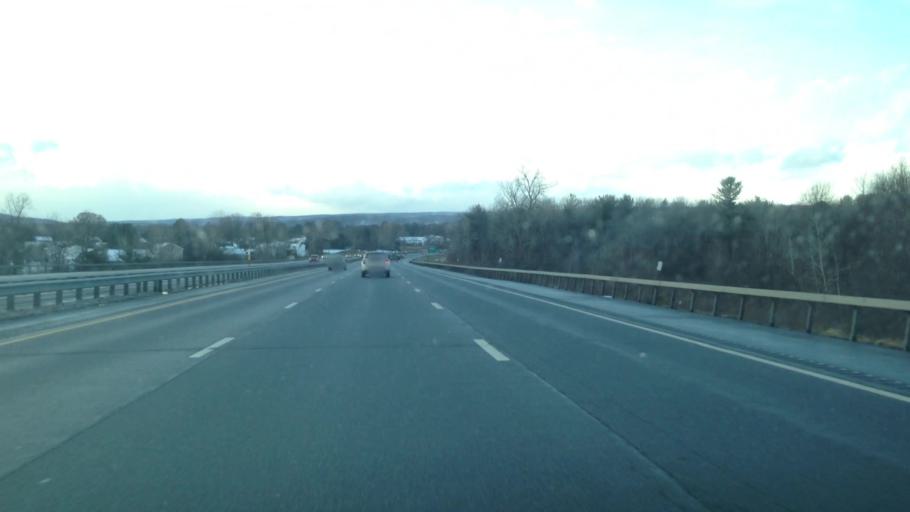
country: US
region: New York
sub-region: Schenectady County
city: Rotterdam
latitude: 42.7751
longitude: -73.9888
